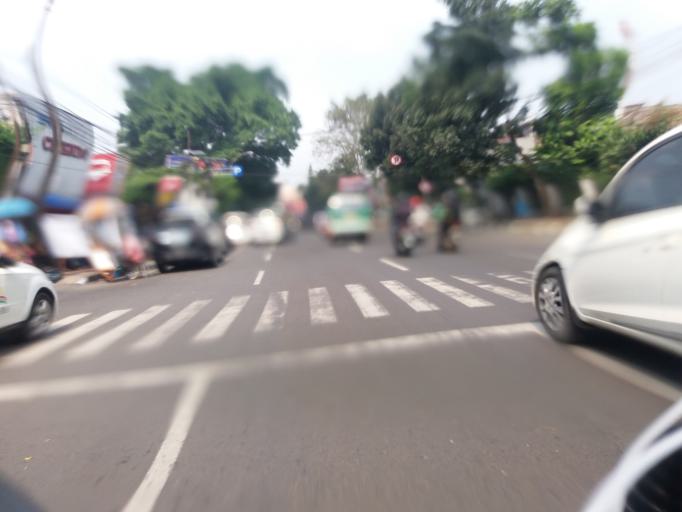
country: ID
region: West Java
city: Bandung
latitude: -6.9103
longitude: 107.6042
